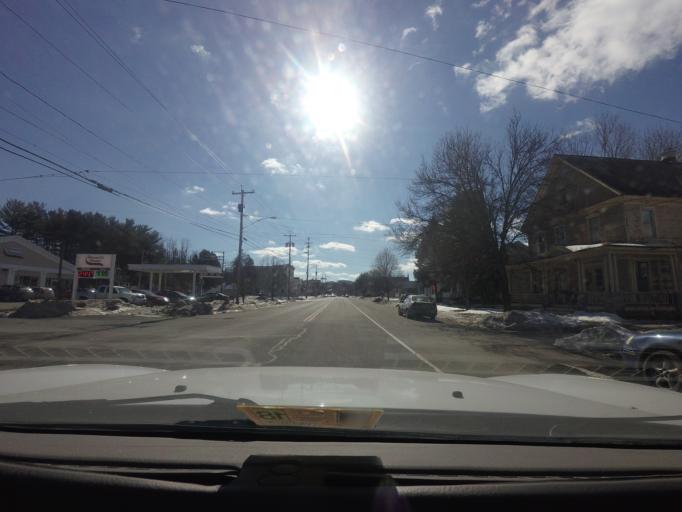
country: US
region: New York
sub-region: Washington County
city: Cambridge
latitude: 43.1752
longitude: -73.3279
